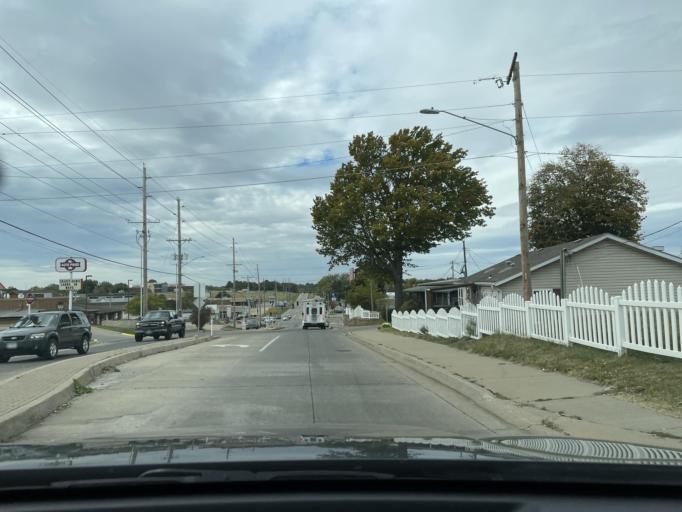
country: US
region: Missouri
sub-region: Buchanan County
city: Saint Joseph
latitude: 39.7698
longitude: -94.8013
